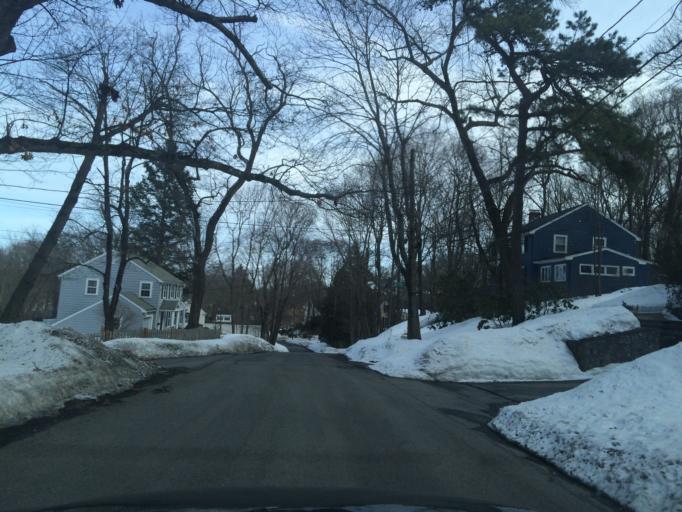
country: US
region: Massachusetts
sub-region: Middlesex County
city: Lexington
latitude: 42.4317
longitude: -71.2107
